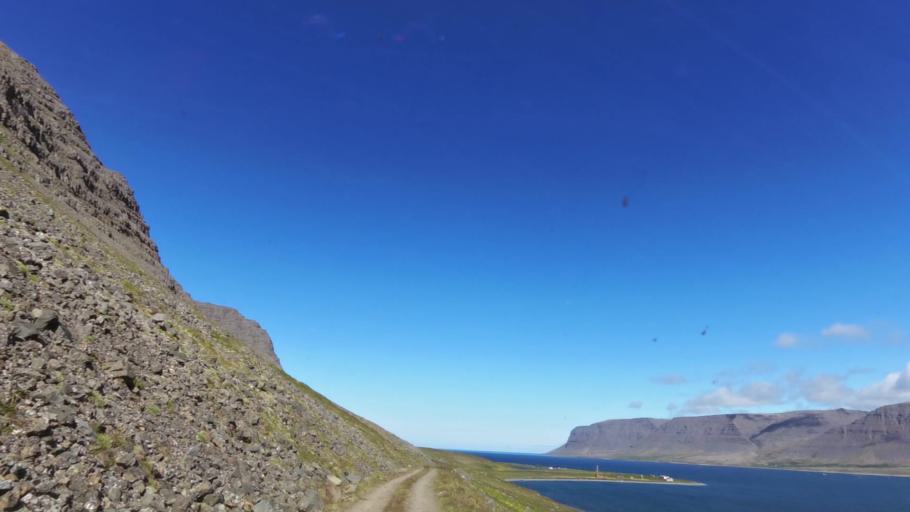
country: IS
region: West
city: Olafsvik
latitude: 65.6334
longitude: -23.9213
